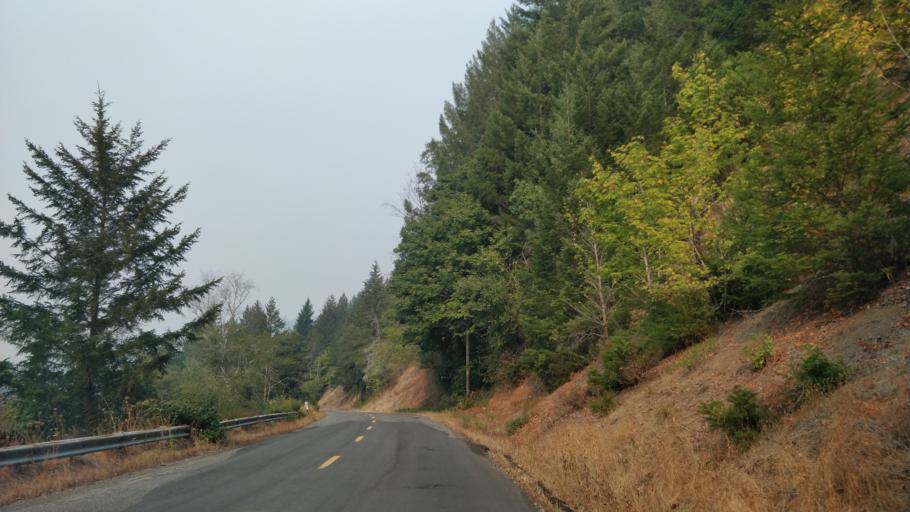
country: US
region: California
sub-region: Humboldt County
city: Rio Dell
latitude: 40.2329
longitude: -124.1380
